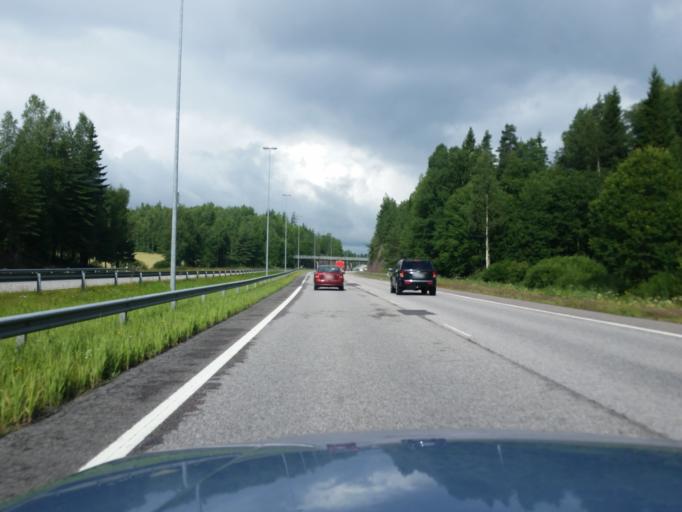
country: FI
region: Uusimaa
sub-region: Helsinki
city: Vihti
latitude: 60.2940
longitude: 24.3172
